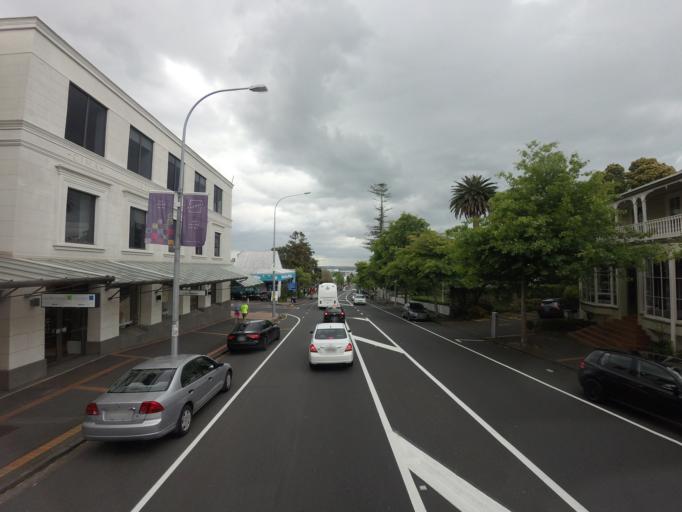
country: NZ
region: Auckland
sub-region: Auckland
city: Auckland
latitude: -36.8580
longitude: 174.7817
